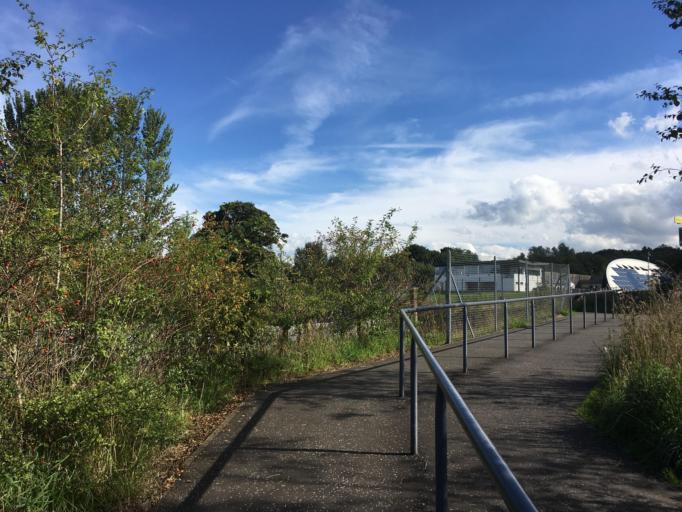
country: GB
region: Scotland
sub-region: Falkirk
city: Larbert
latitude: 56.0022
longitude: -3.8427
